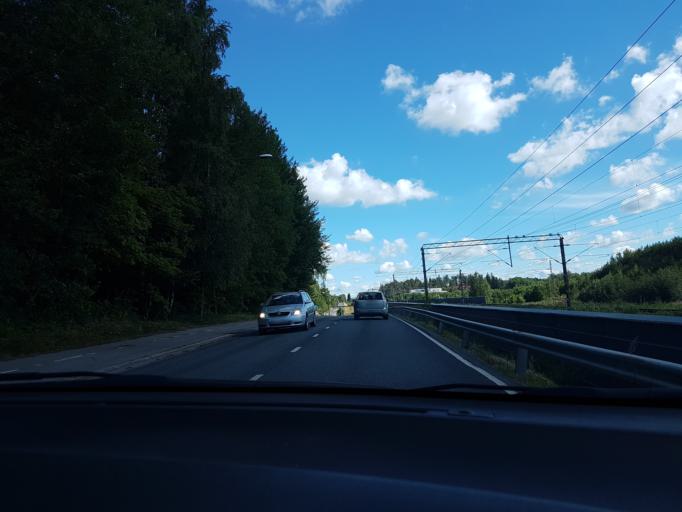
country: FI
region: Uusimaa
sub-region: Helsinki
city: Kerava
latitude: 60.3731
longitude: 25.0947
